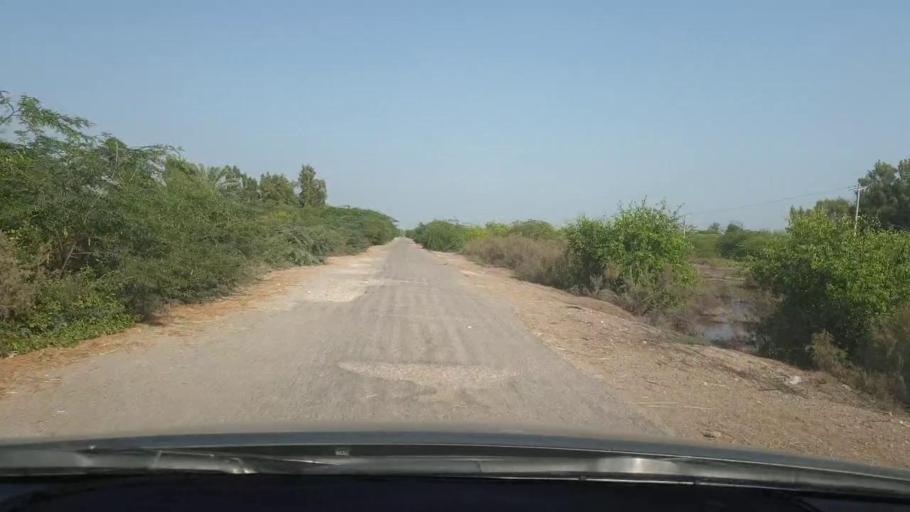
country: PK
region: Sindh
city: Naukot
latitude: 24.7610
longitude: 69.2202
